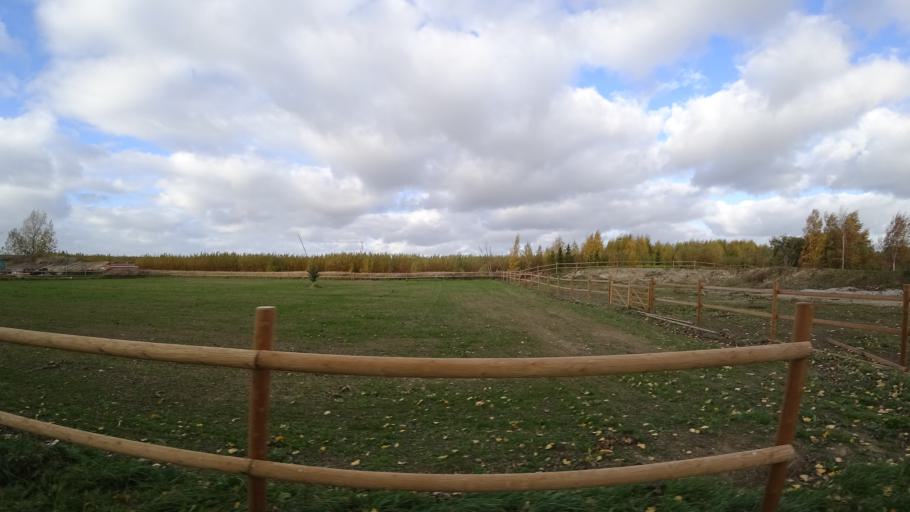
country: SE
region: Skane
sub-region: Staffanstorps Kommun
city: Staffanstorp
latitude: 55.6273
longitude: 13.2072
